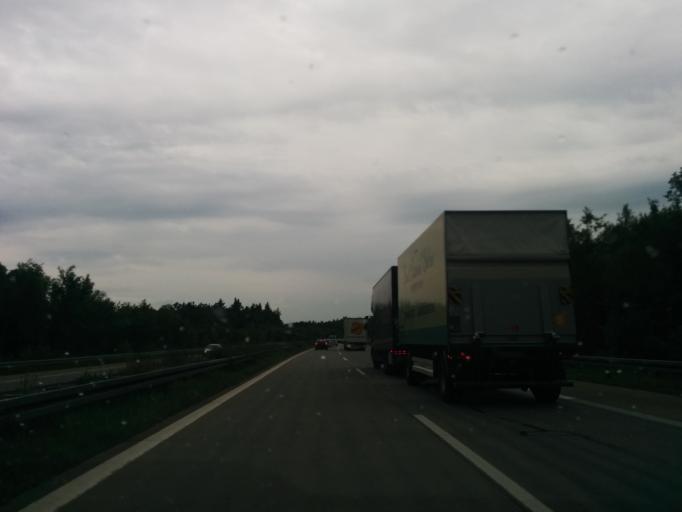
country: DE
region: Bavaria
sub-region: Regierungsbezirk Mittelfranken
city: Ohrenbach
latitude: 49.4895
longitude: 10.2050
